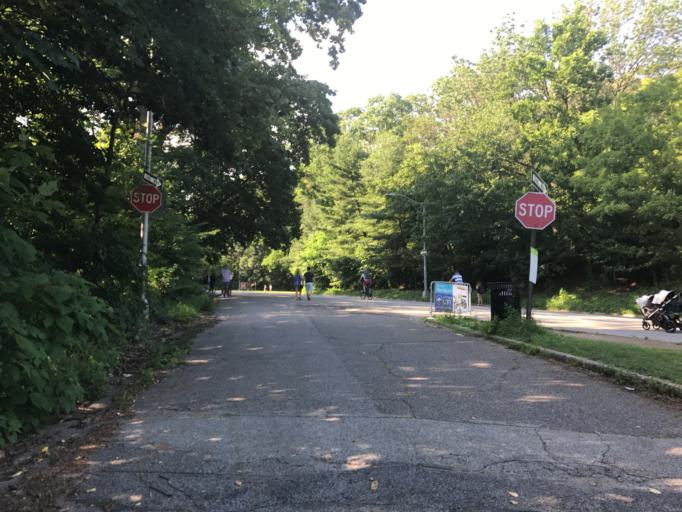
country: US
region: New York
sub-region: Kings County
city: Brooklyn
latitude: 40.6609
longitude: -73.9646
